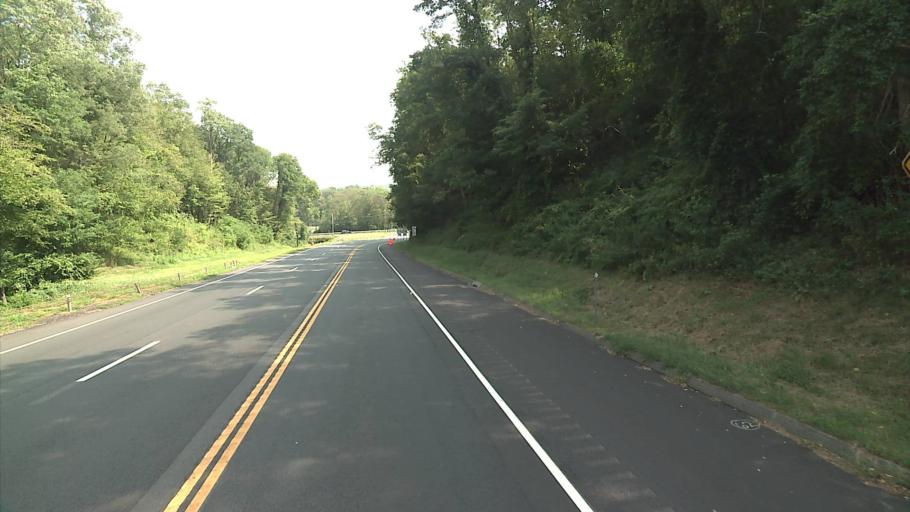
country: US
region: Connecticut
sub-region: Middlesex County
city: East Haddam
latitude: 41.4427
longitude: -72.4732
